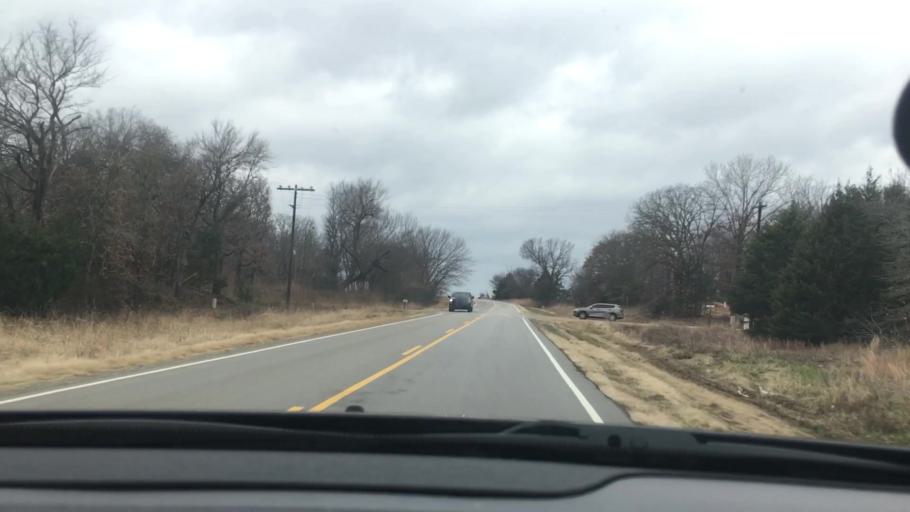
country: US
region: Oklahoma
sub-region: Atoka County
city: Atoka
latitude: 34.3792
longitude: -96.2845
